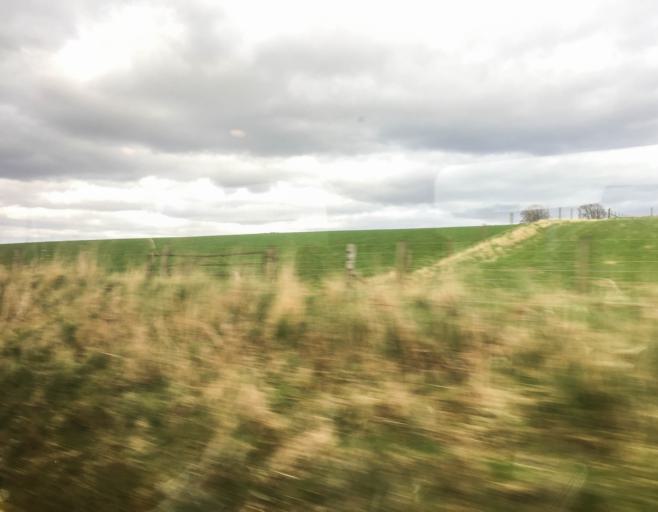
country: GB
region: Scotland
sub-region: South Lanarkshire
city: Carnwath
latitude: 55.6519
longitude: -3.6336
